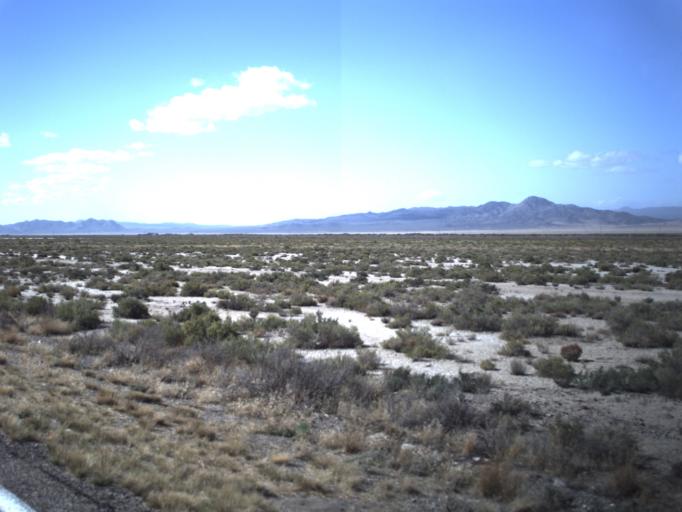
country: US
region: Utah
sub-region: Beaver County
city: Milford
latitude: 38.6164
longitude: -112.9856
